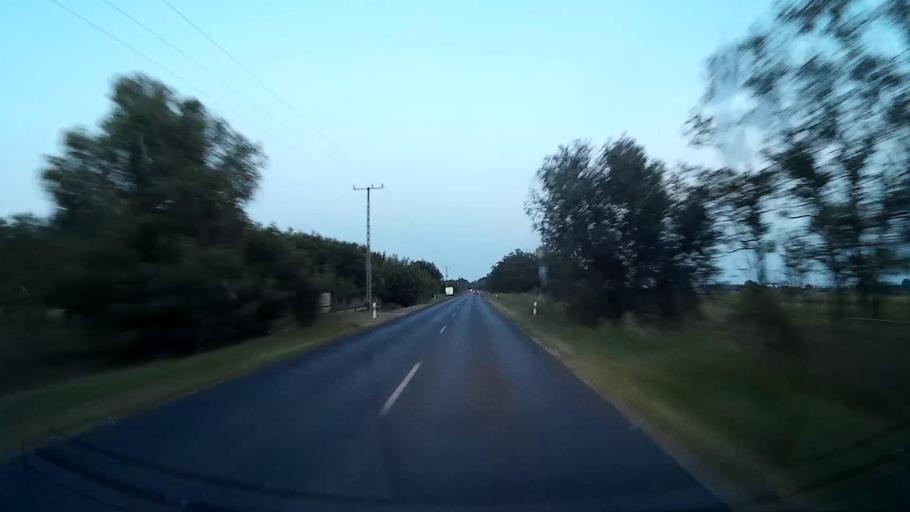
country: HU
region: Pest
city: Cegled
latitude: 47.1907
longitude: 19.7356
